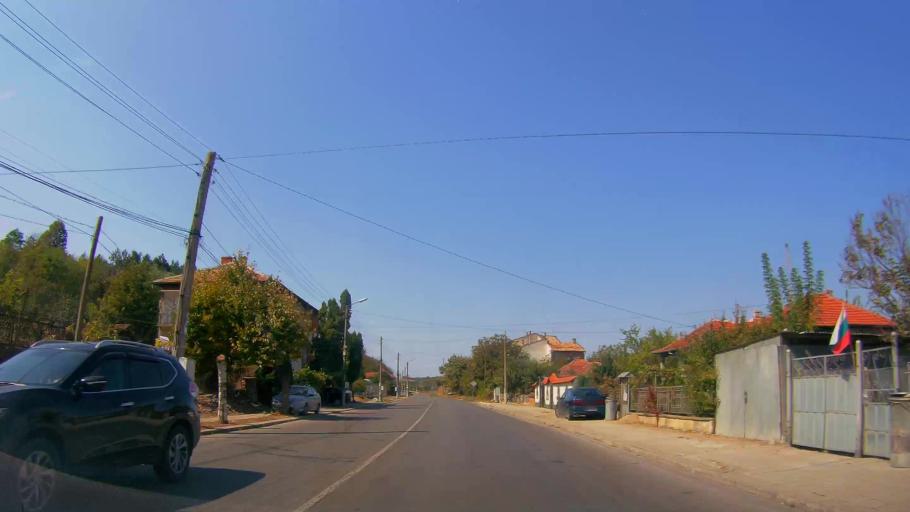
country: BG
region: Razgrad
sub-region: Obshtina Tsar Kaloyan
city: Tsar Kaloyan
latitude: 43.6114
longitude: 26.2322
